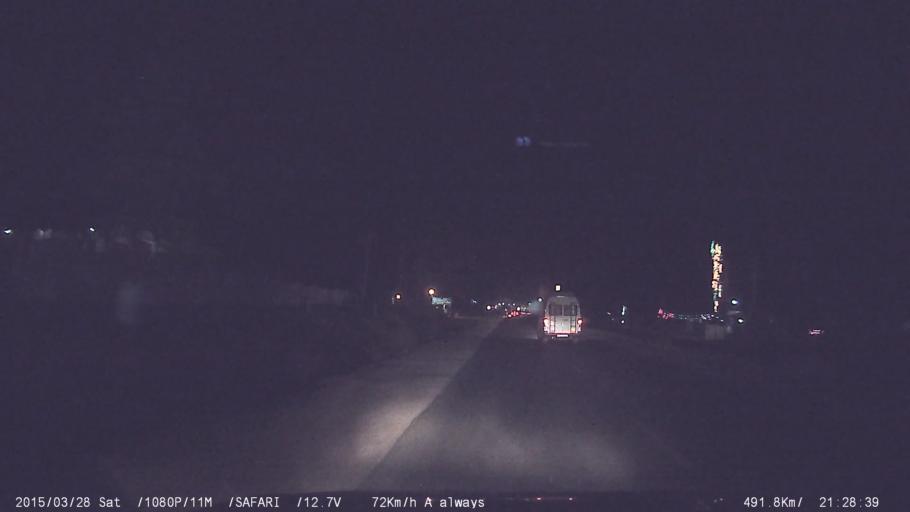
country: IN
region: Karnataka
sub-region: Ramanagara
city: Ramanagaram
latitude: 12.8236
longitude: 77.4109
